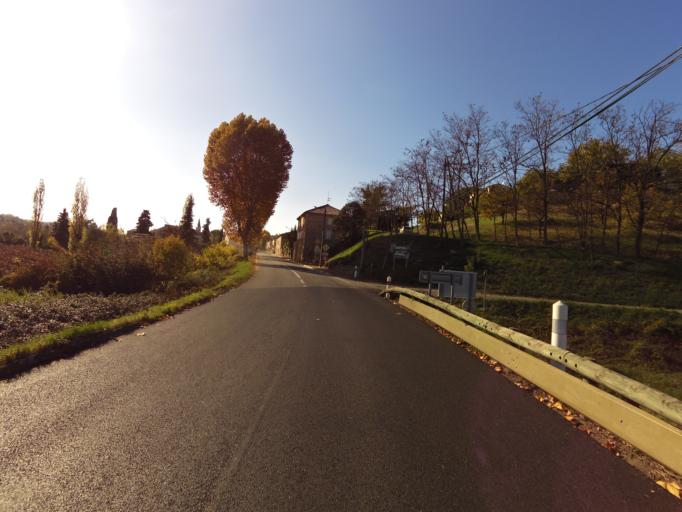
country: FR
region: Rhone-Alpes
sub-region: Departement de l'Ardeche
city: Largentiere
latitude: 44.5213
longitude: 4.3294
